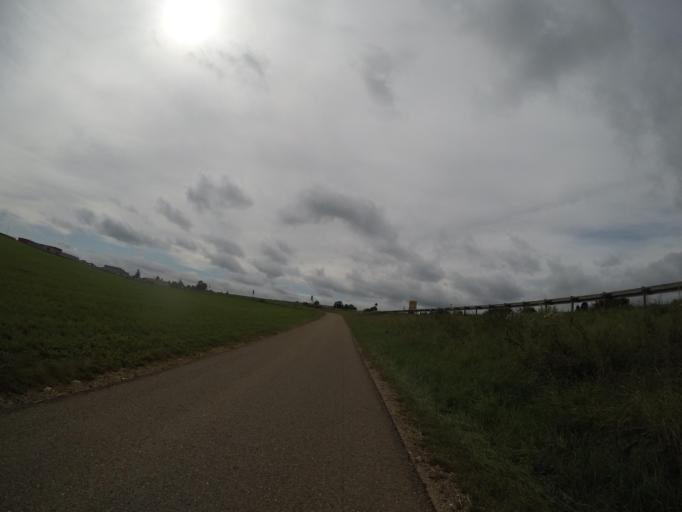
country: DE
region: Baden-Wuerttemberg
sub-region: Tuebingen Region
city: Laichingen
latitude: 48.4540
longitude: 9.6632
